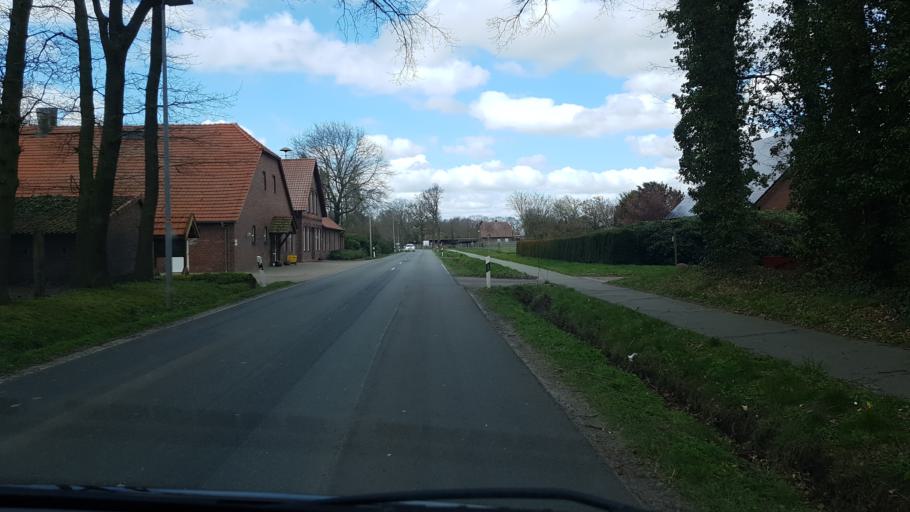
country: DE
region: Lower Saxony
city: Edewecht
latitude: 53.1192
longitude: 7.9417
